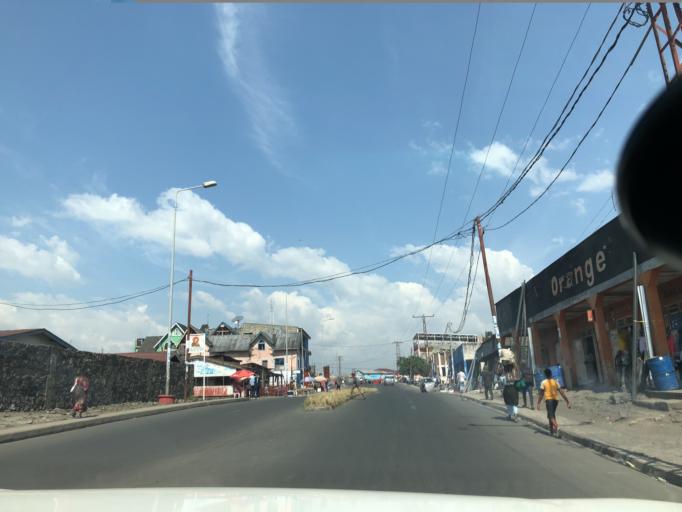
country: CD
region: Nord Kivu
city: Goma
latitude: -1.6570
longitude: 29.1955
